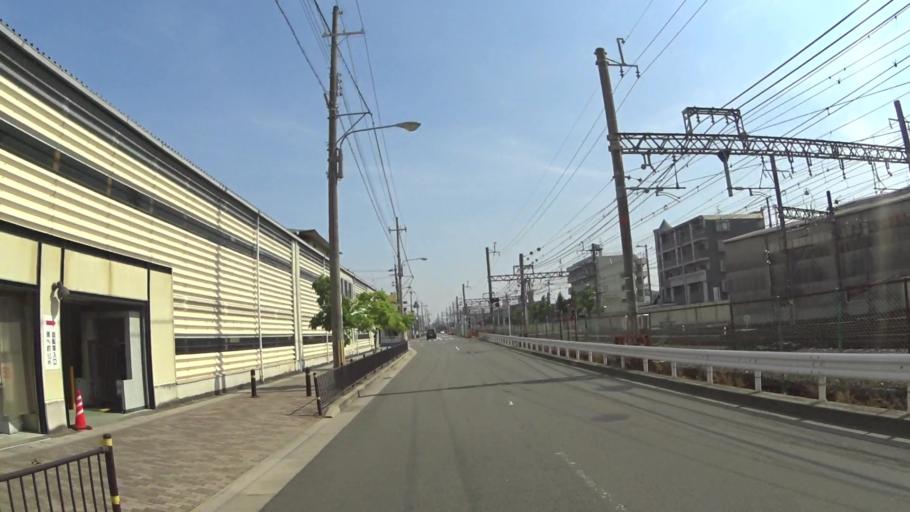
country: JP
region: Kyoto
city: Muko
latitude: 34.9773
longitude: 135.7032
